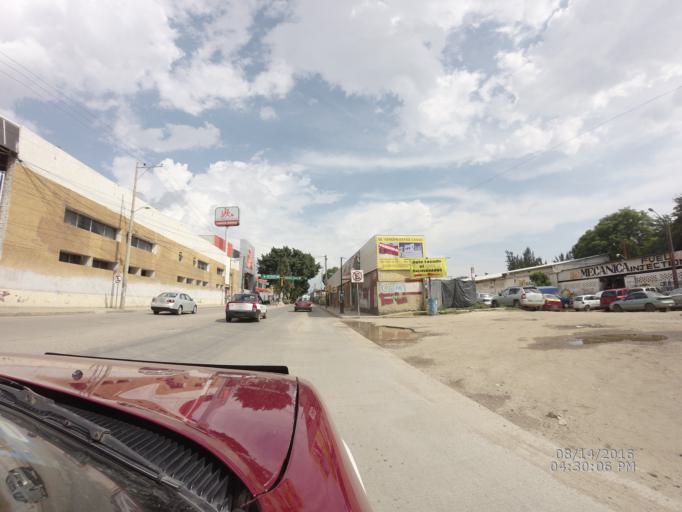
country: MX
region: Oaxaca
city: Oaxaca de Juarez
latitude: 17.0792
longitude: -96.7430
